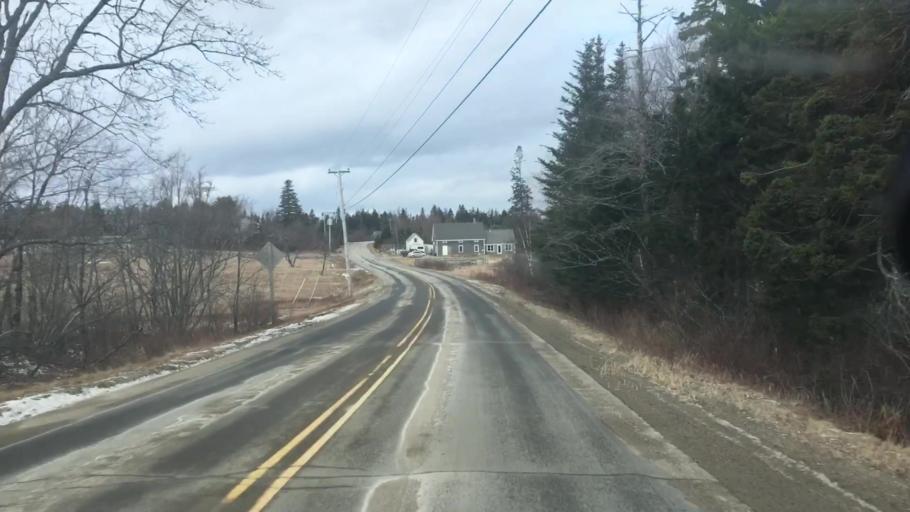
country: US
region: Maine
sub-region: Washington County
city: Machias
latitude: 44.6155
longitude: -67.4792
